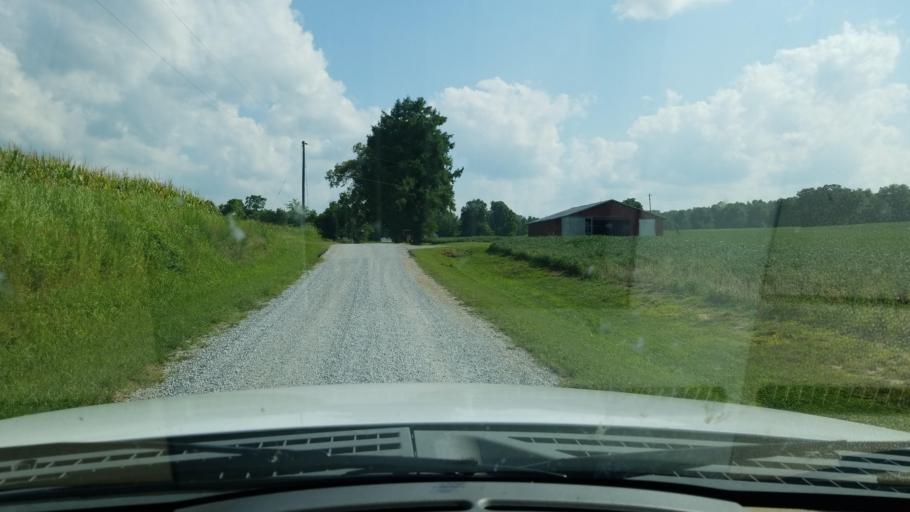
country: US
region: Illinois
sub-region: Saline County
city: Eldorado
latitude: 37.8437
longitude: -88.4802
